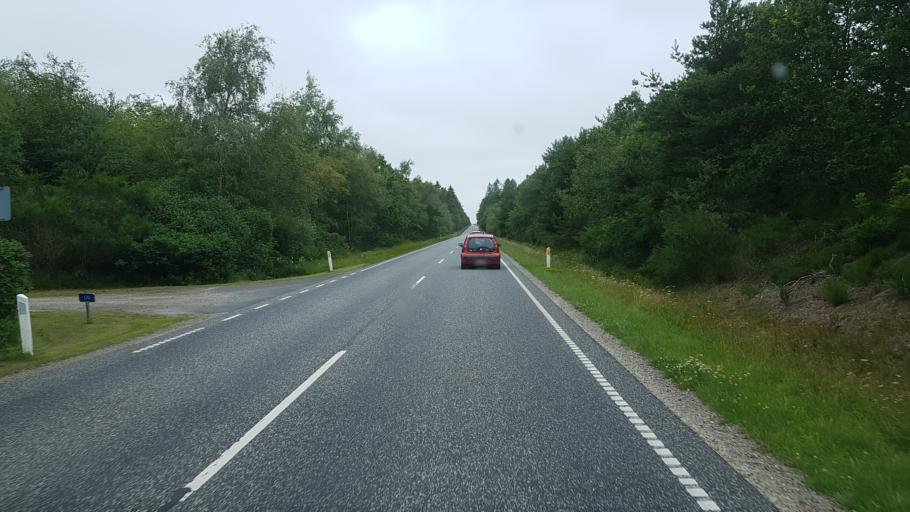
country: DK
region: Central Jutland
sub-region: Lemvig Kommune
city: Lemvig
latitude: 56.4626
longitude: 8.3269
